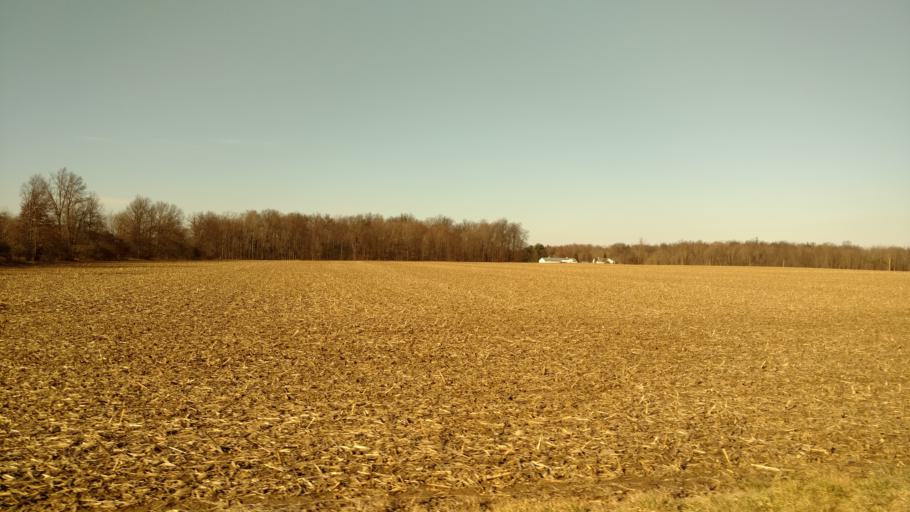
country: US
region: Ohio
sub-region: Crawford County
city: Galion
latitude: 40.7117
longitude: -82.7502
